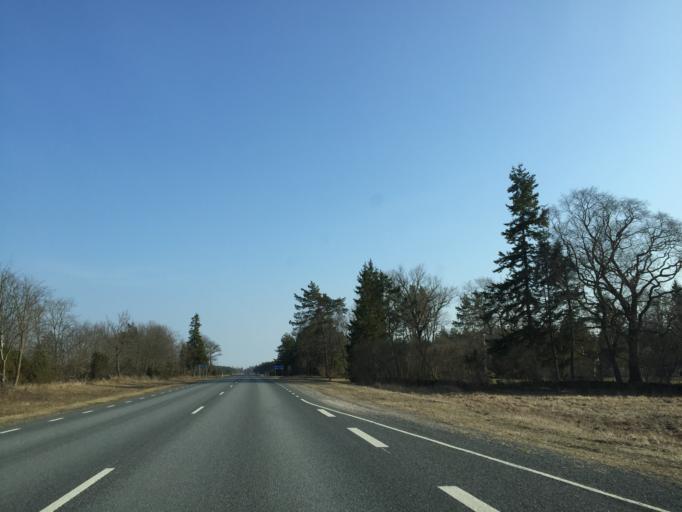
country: EE
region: Saare
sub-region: Orissaare vald
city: Orissaare
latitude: 58.5918
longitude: 23.3333
